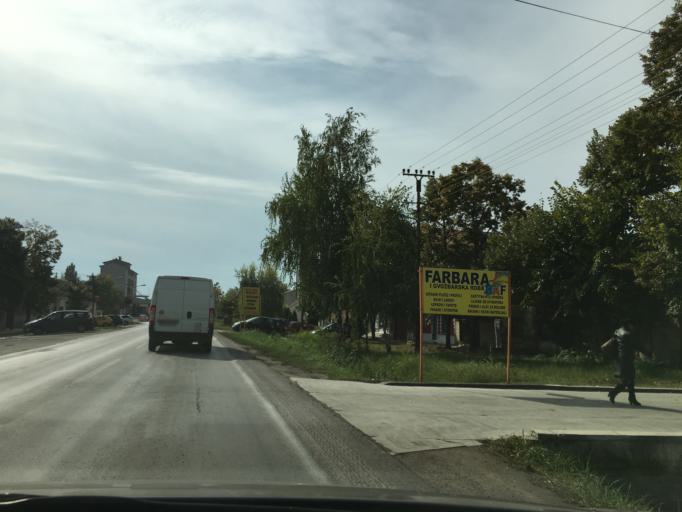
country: RS
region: Autonomna Pokrajina Vojvodina
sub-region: Juznobacki Okrug
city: Temerin
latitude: 45.4024
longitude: 19.8855
